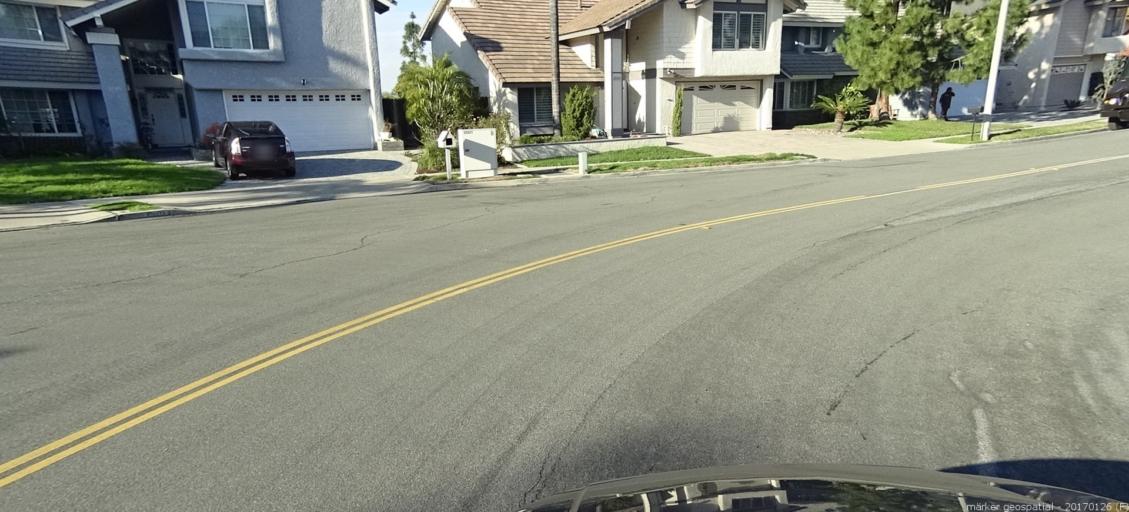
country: US
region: California
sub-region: Orange County
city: Lake Forest
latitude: 33.6442
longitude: -117.6909
